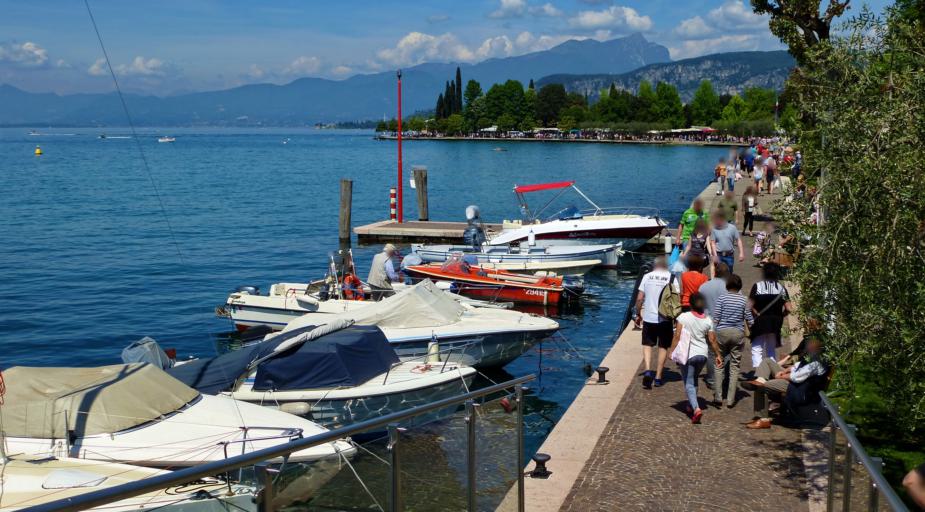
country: IT
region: Veneto
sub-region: Provincia di Verona
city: Bardolino
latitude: 45.5474
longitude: 10.7188
